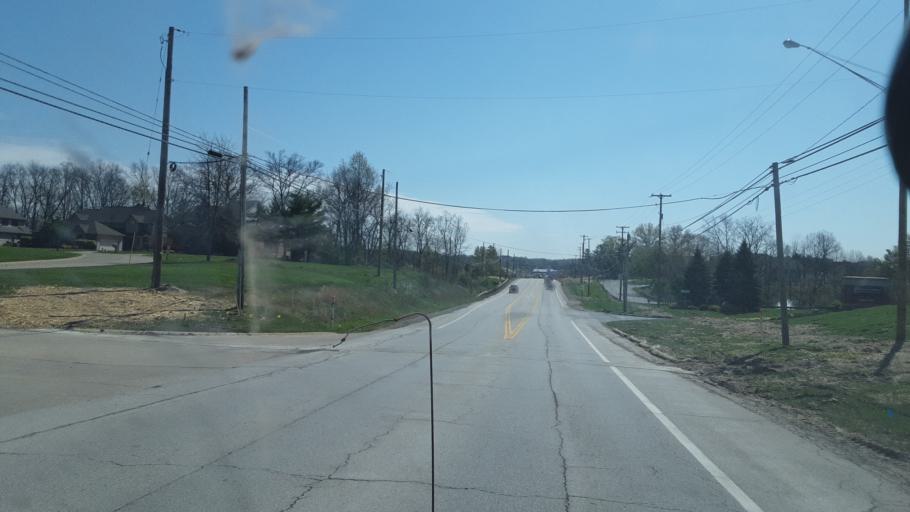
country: US
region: Ohio
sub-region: Medina County
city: Medina
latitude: 41.1379
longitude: -81.8292
